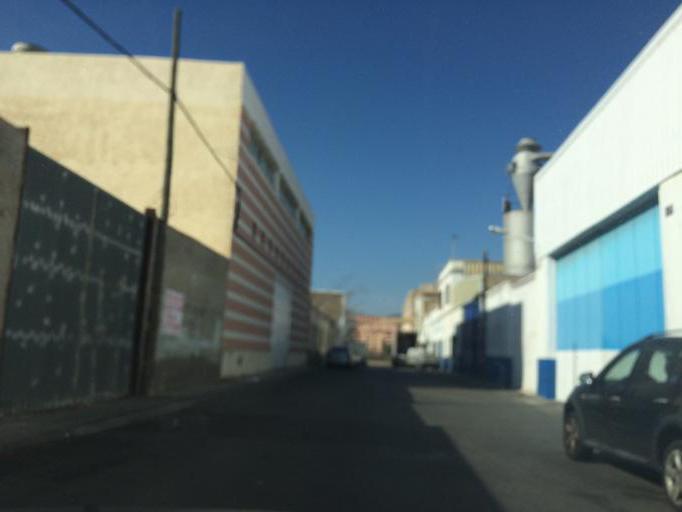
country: ES
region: Andalusia
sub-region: Provincia de Almeria
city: Almeria
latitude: 36.8413
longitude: -2.4376
